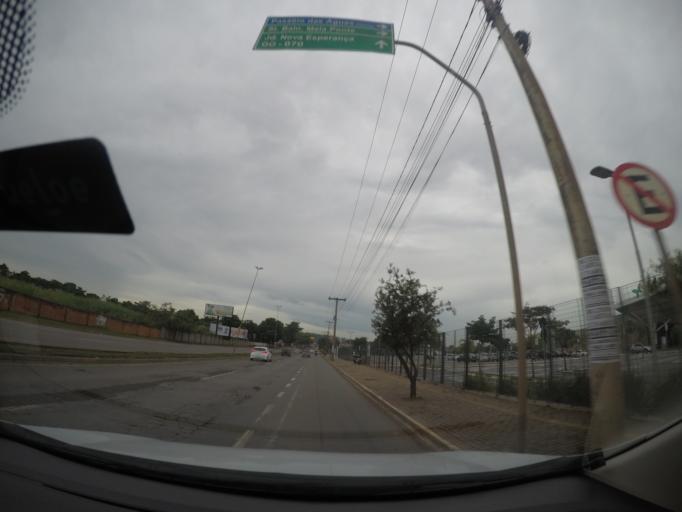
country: BR
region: Goias
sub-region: Goiania
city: Goiania
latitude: -16.6320
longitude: -49.2787
